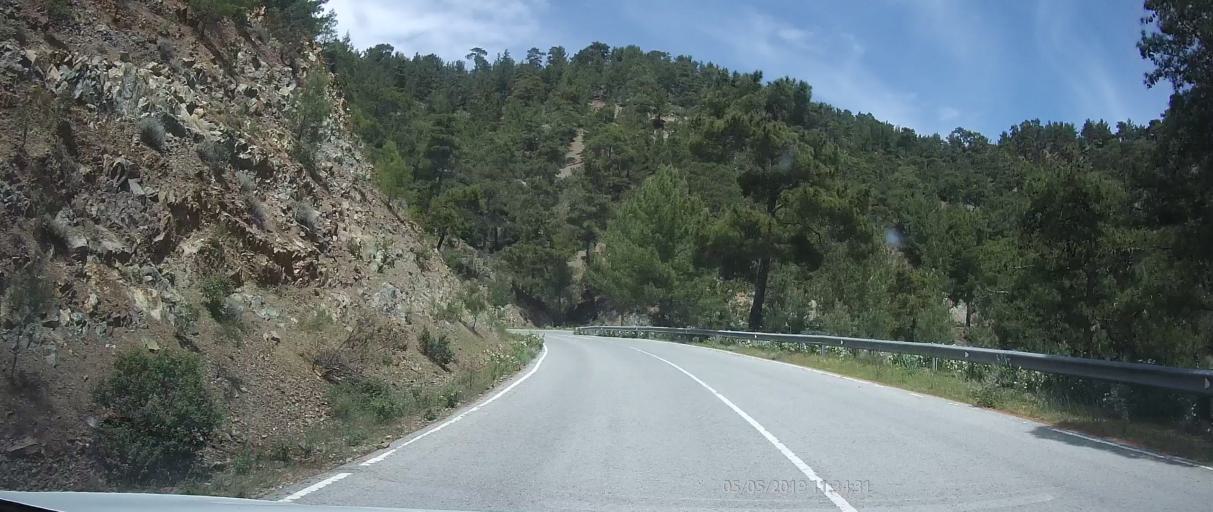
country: CY
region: Lefkosia
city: Kato Pyrgos
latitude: 34.9667
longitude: 32.6481
